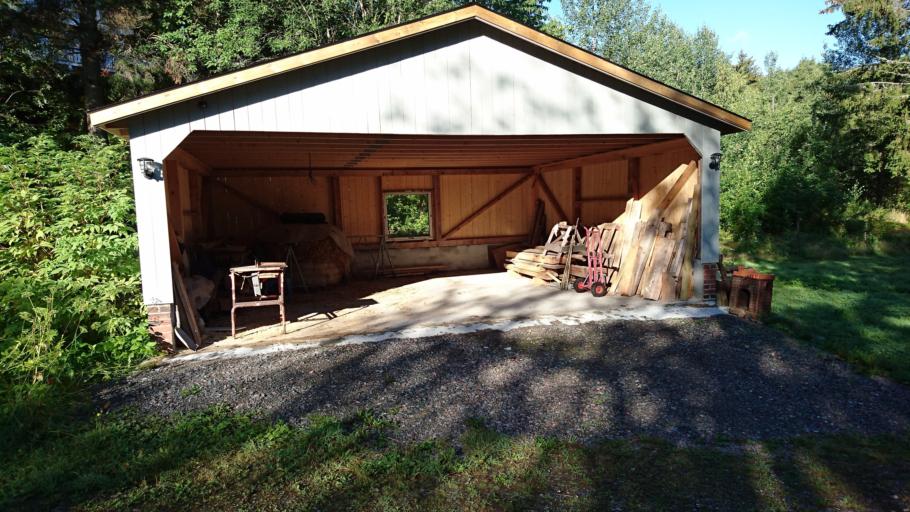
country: NO
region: Telemark
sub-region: Nome
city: Ulefoss
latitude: 59.2754
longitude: 9.3474
